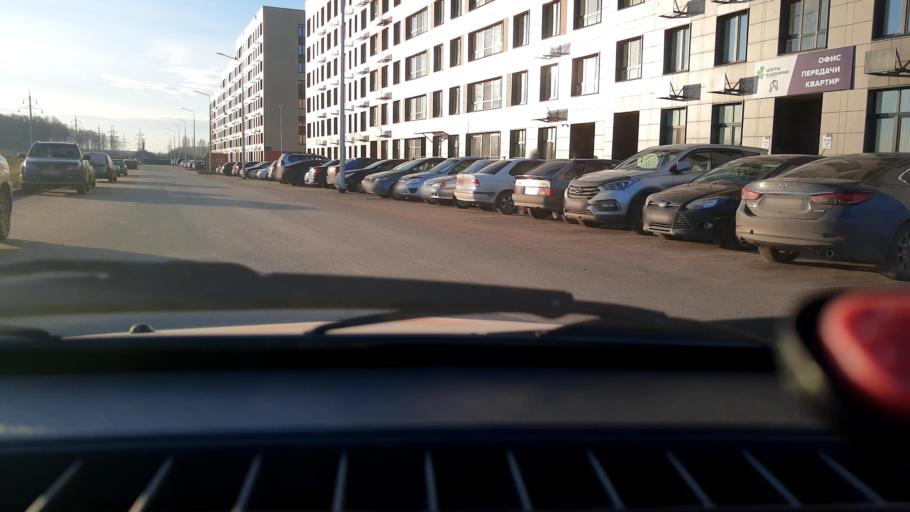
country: RU
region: Bashkortostan
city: Ufa
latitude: 54.6756
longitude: 55.9201
